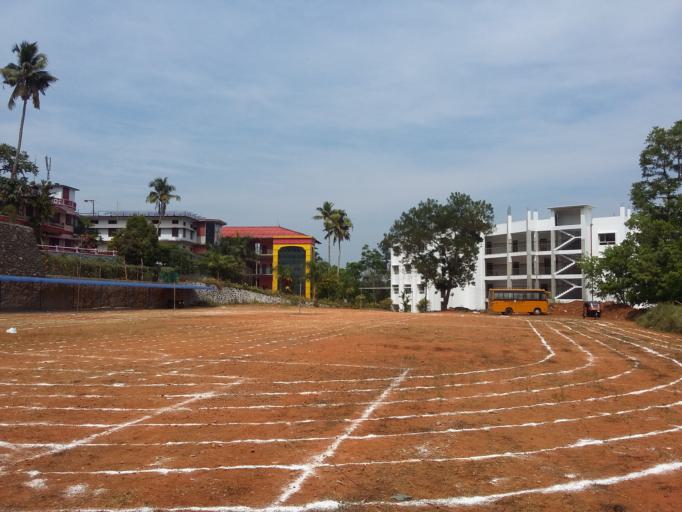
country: IN
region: Kerala
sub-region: Kottayam
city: Palackattumala
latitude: 9.8685
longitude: 76.6447
